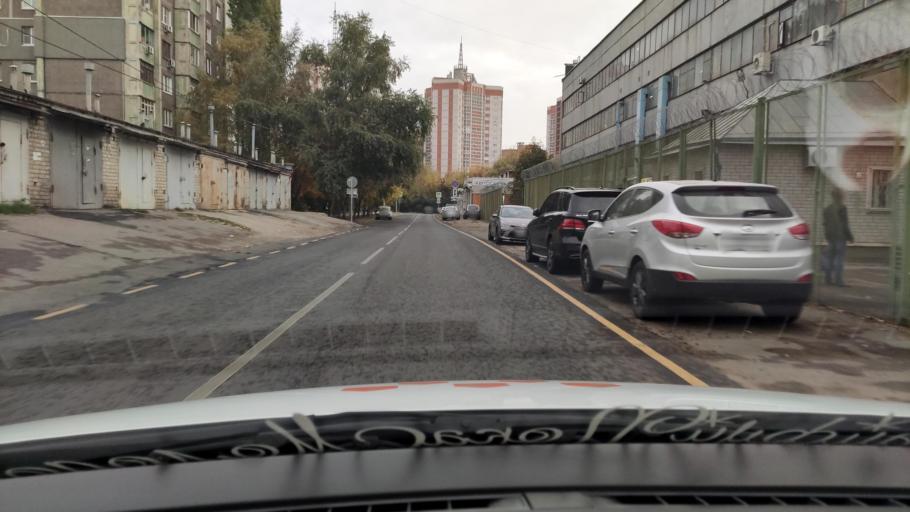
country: RU
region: Voronezj
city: Voronezh
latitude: 51.6687
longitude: 39.1821
